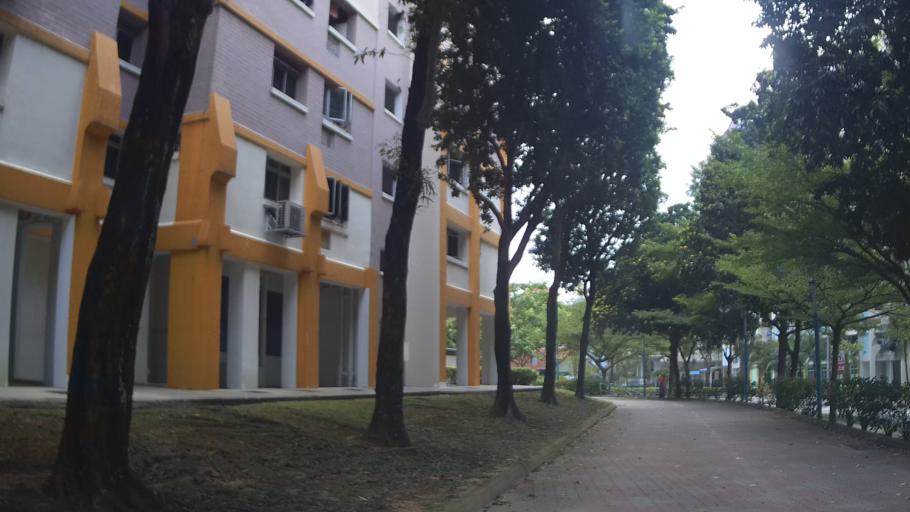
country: MY
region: Johor
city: Johor Bahru
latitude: 1.4424
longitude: 103.7986
